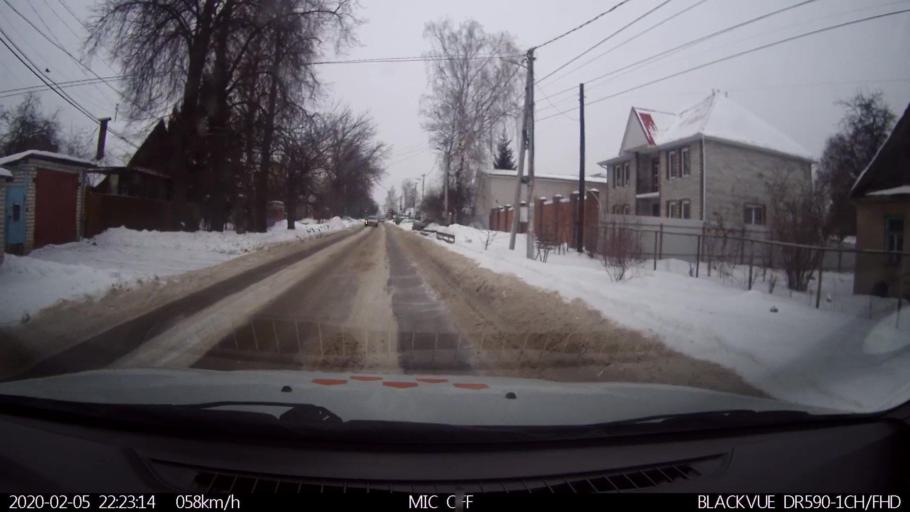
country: RU
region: Nizjnij Novgorod
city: Pervomaysk
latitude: 54.7657
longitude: 44.0254
